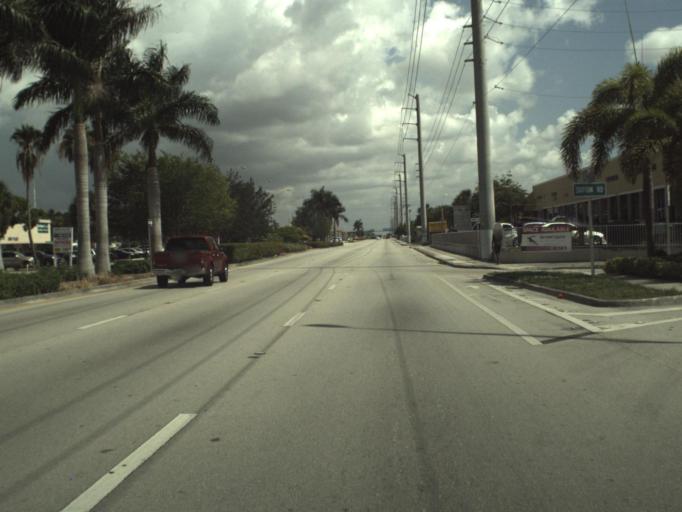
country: US
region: Florida
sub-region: Broward County
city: Miami Gardens
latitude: 25.9765
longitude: -80.2061
